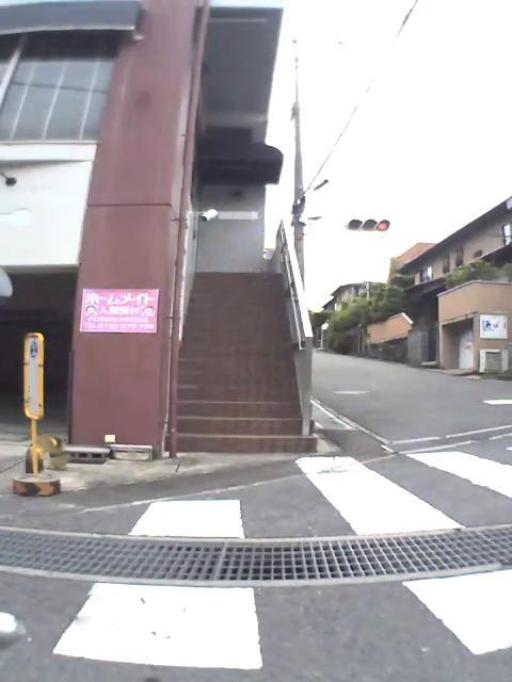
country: JP
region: Osaka
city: Hirakata
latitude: 34.7998
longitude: 135.6458
